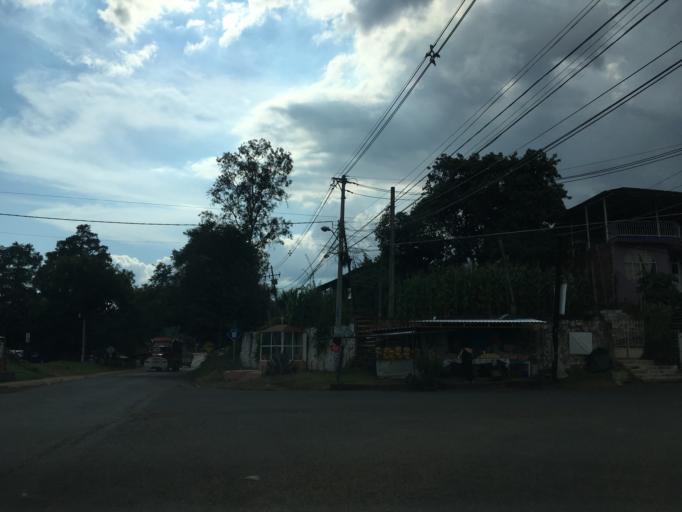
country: MX
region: Michoacan
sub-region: Ziracuaretiro
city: Patuan
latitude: 19.4170
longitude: -101.9181
